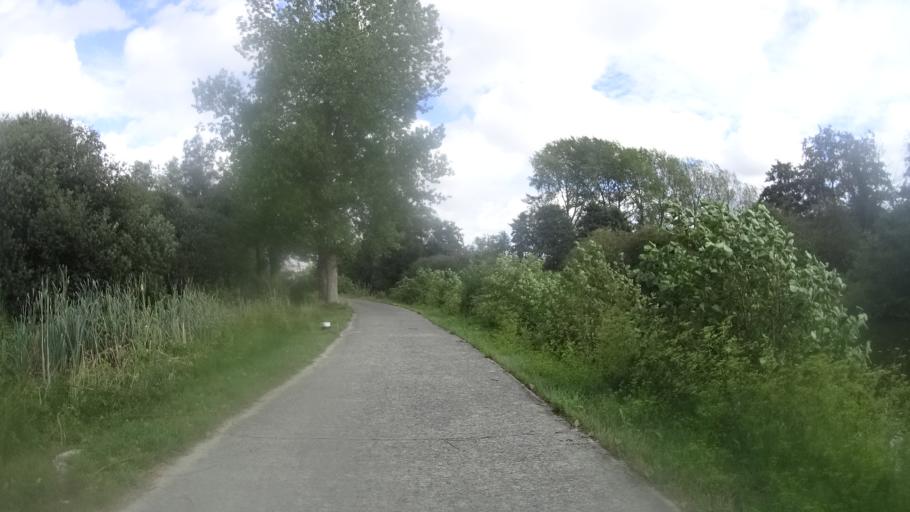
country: BE
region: Wallonia
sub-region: Province du Hainaut
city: Merbes-le-Chateau
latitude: 50.3187
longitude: 4.1729
